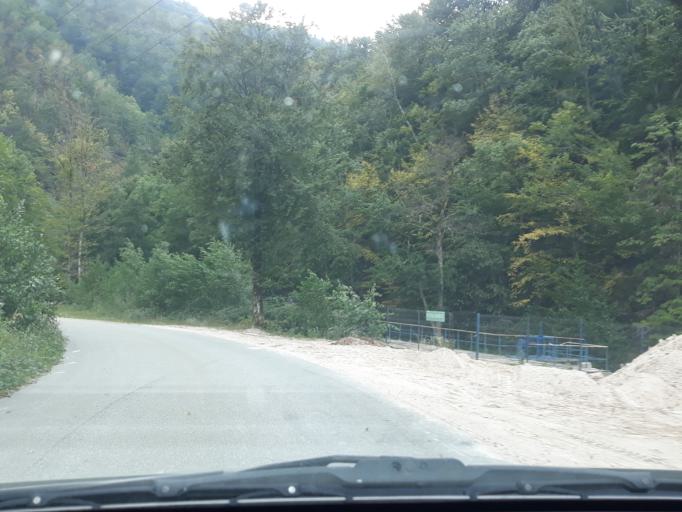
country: RO
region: Bihor
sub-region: Comuna Pietroasa
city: Pietroasa
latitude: 46.5884
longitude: 22.6021
